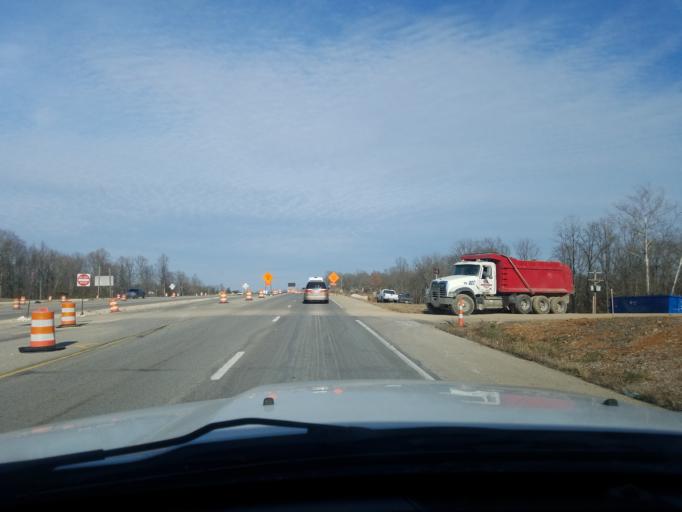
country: US
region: Indiana
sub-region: Monroe County
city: Bloomington
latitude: 39.2536
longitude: -86.5277
